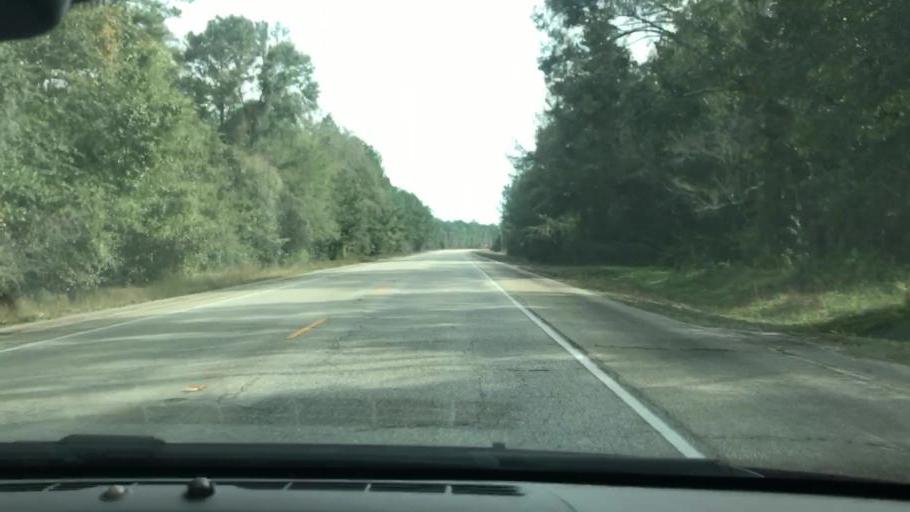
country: US
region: Mississippi
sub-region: Pearl River County
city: Nicholson
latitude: 30.5218
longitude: -89.8468
